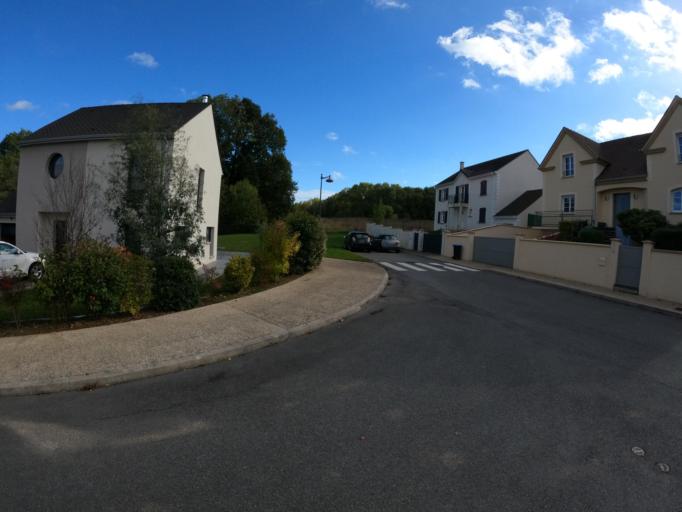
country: FR
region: Ile-de-France
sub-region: Departement de Seine-et-Marne
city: Montry
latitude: 48.8897
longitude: 2.8155
